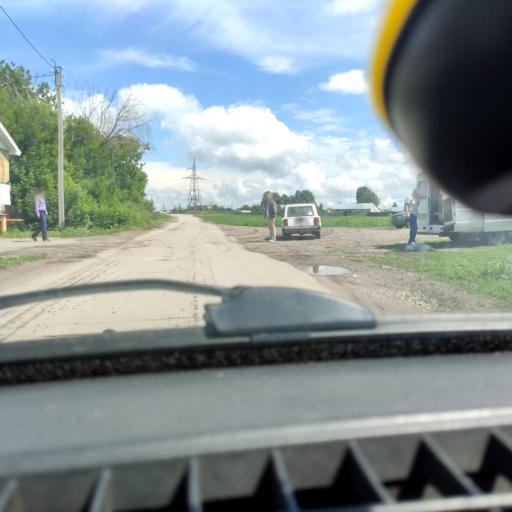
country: RU
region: Samara
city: Zhigulevsk
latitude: 53.5559
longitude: 49.5266
